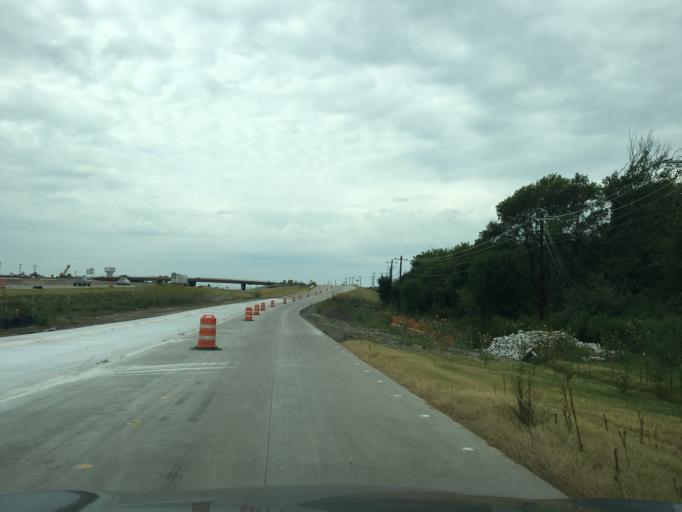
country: US
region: Texas
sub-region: Collin County
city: Anna
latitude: 33.3665
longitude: -96.5833
